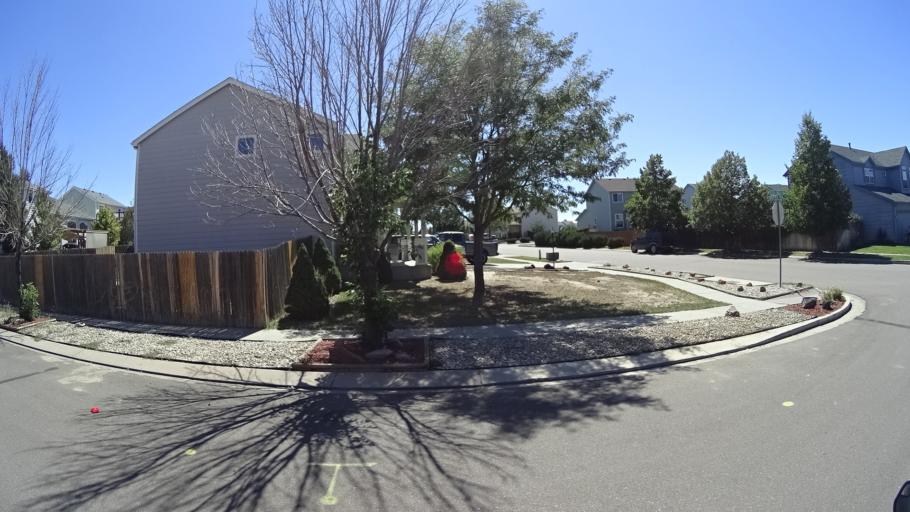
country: US
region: Colorado
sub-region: El Paso County
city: Security-Widefield
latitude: 38.7874
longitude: -104.7348
